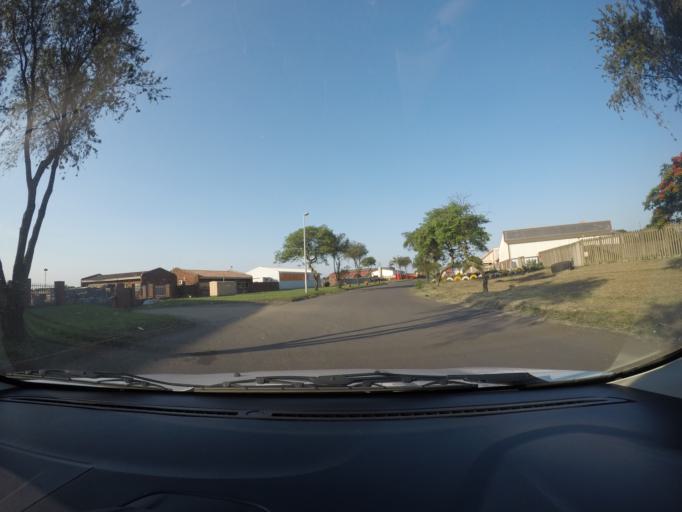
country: ZA
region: KwaZulu-Natal
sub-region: uThungulu District Municipality
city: Richards Bay
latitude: -28.7629
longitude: 32.0047
